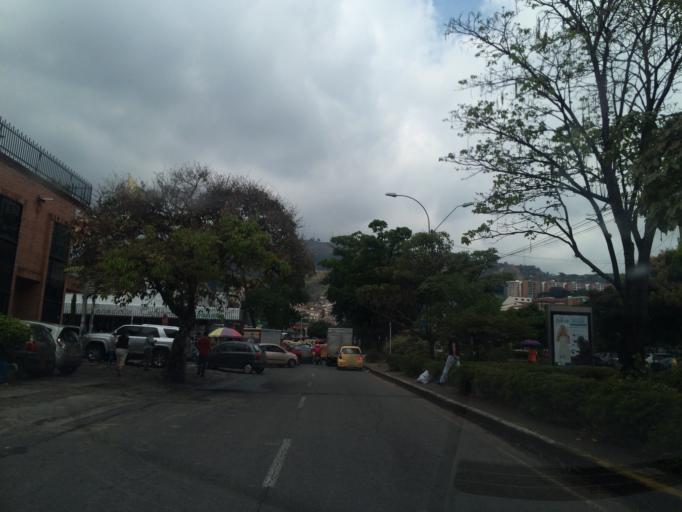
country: CO
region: Valle del Cauca
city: Cali
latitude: 3.4239
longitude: -76.5455
